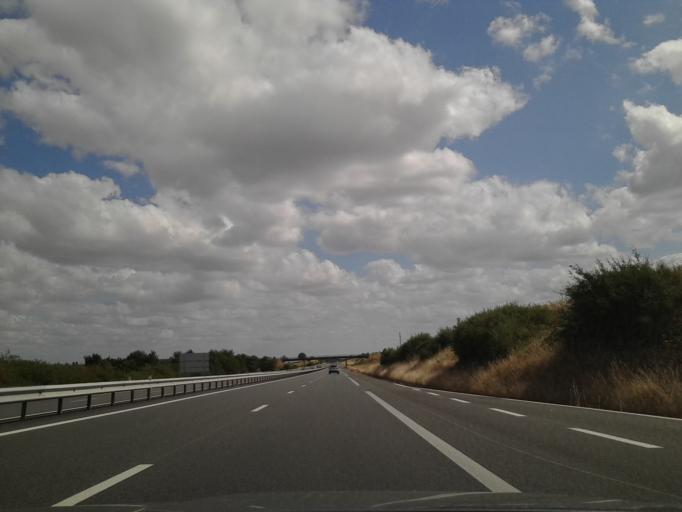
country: FR
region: Centre
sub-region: Departement du Cher
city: Orval
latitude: 46.7104
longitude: 2.4609
